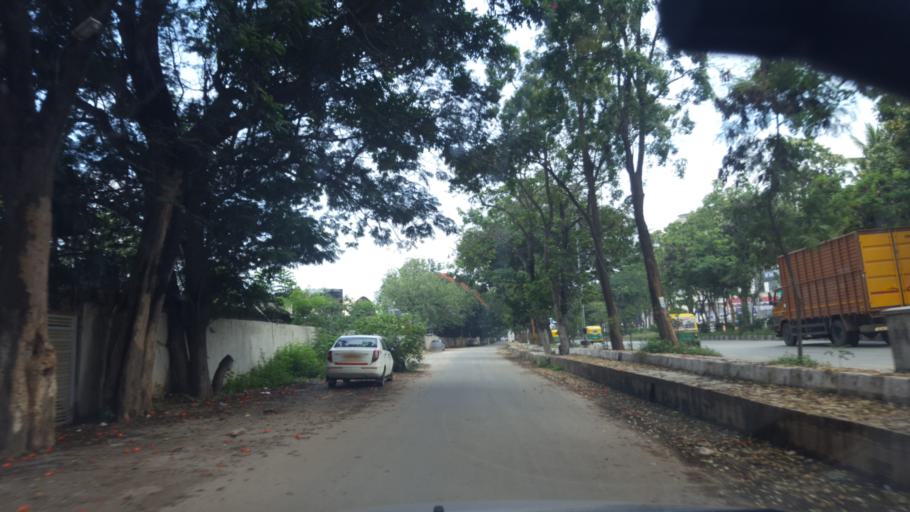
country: IN
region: Karnataka
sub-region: Bangalore Urban
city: Yelahanka
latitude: 13.0438
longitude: 77.6074
